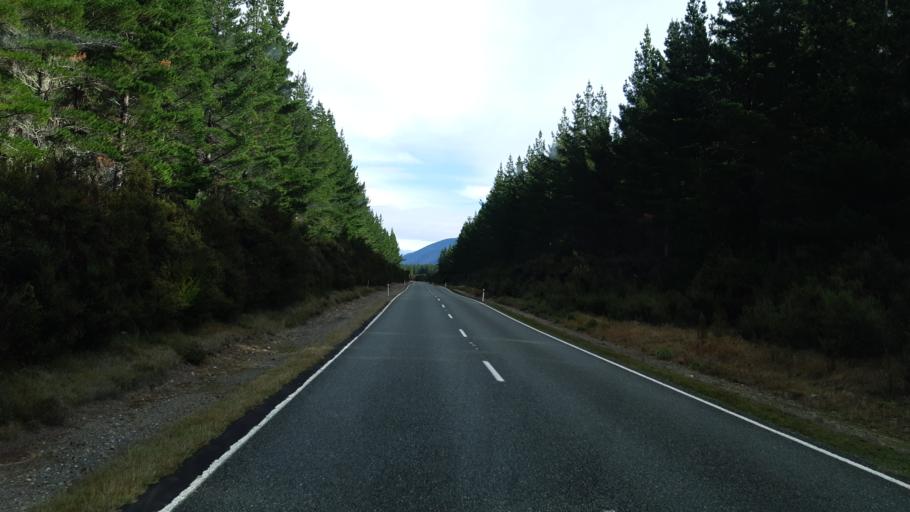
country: NZ
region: Tasman
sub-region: Tasman District
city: Wakefield
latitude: -41.7206
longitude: 173.0628
